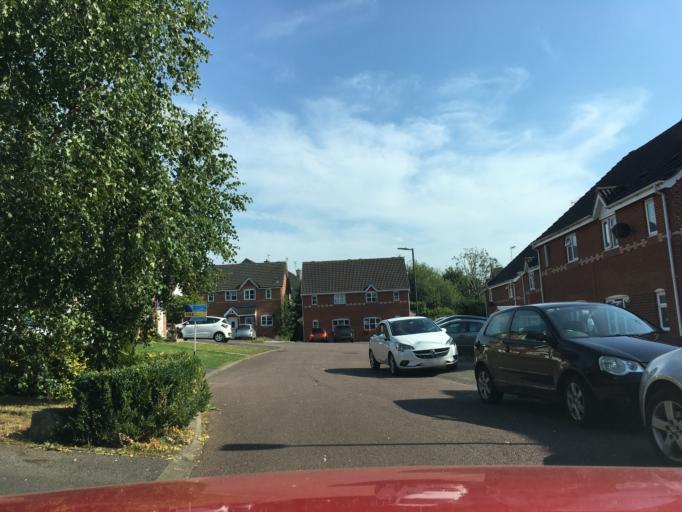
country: GB
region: England
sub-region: Gloucestershire
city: Dursley
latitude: 51.6978
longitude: -2.3573
